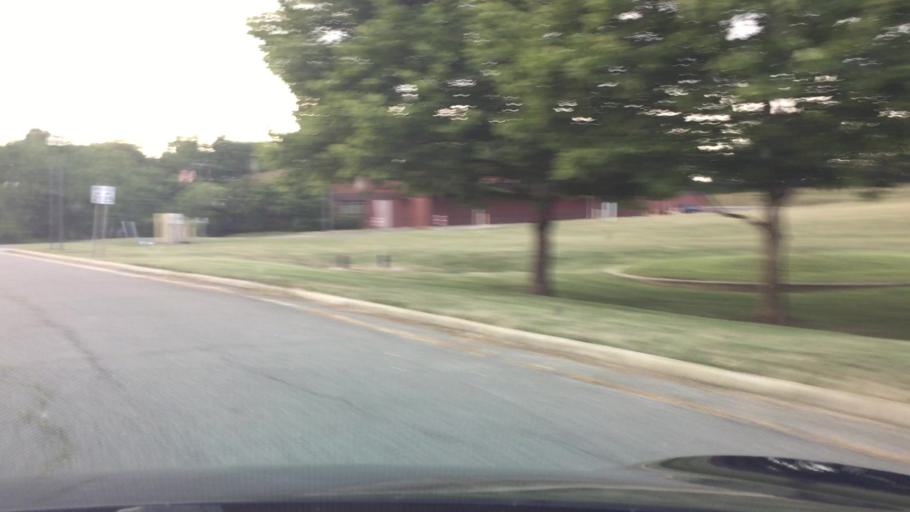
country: US
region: Virginia
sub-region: Pulaski County
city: Dublin
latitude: 37.0926
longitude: -80.6865
